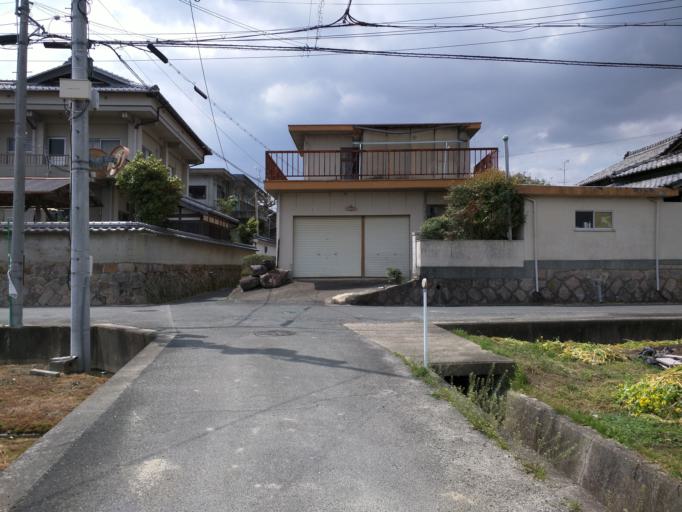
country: JP
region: Kyoto
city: Tanabe
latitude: 34.7656
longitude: 135.7998
